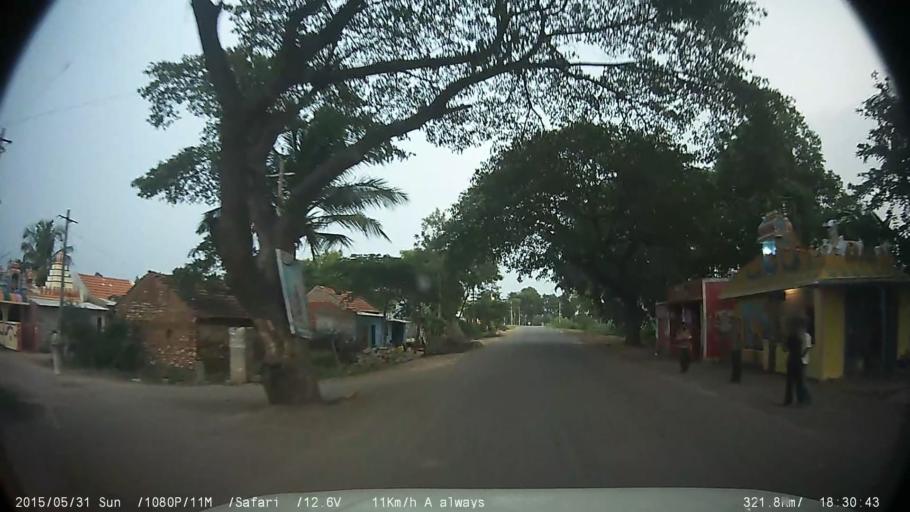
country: IN
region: Karnataka
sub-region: Mysore
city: Nanjangud
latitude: 12.1269
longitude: 76.7396
